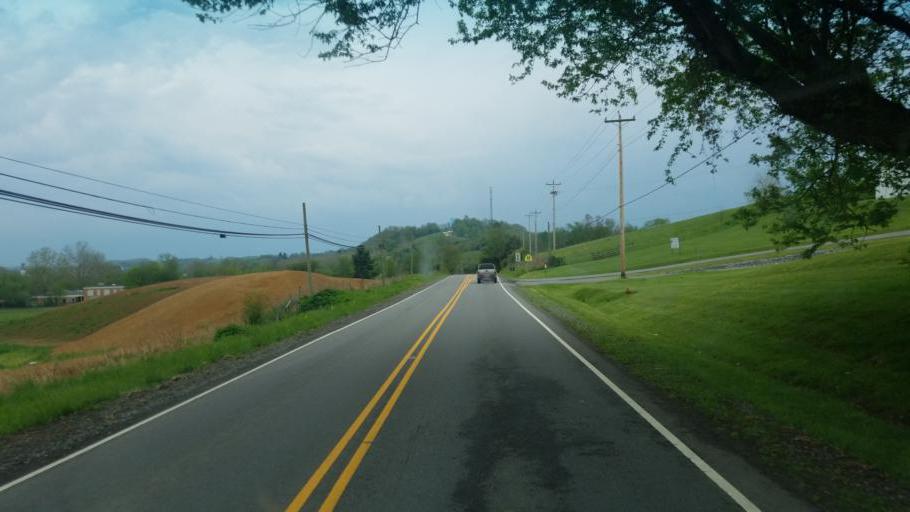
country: US
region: Virginia
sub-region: Smyth County
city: Chilhowie
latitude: 36.8143
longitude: -81.6567
